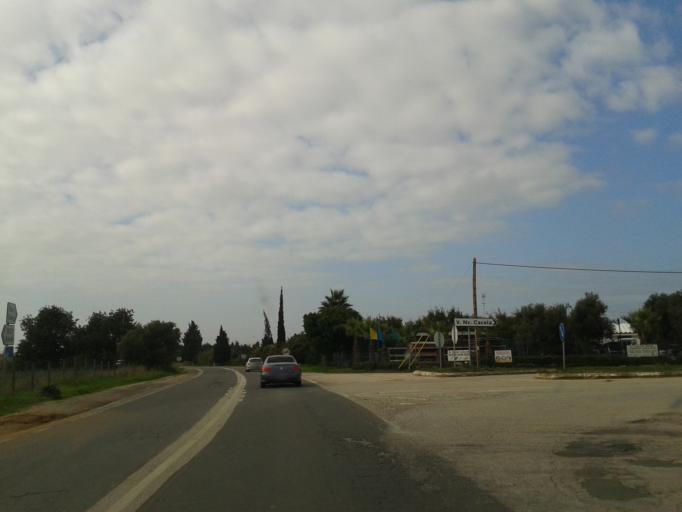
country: PT
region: Faro
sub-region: Vila Real de Santo Antonio
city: Monte Gordo
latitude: 37.1784
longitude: -7.5234
